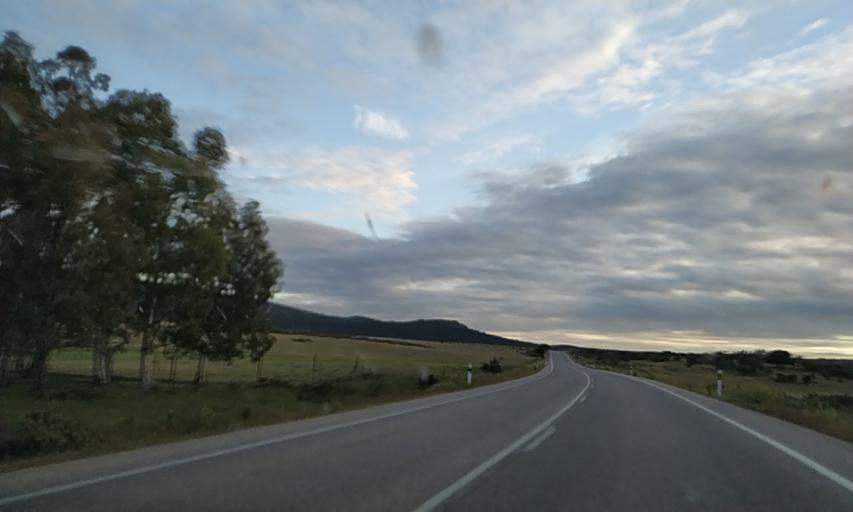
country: ES
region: Extremadura
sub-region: Provincia de Caceres
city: Malpartida de Caceres
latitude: 39.3259
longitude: -6.4952
